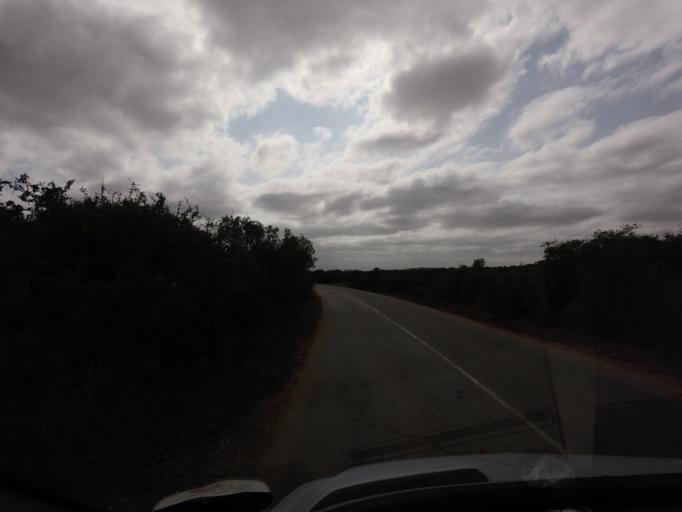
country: ZA
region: Eastern Cape
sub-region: Cacadu District Municipality
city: Kirkwood
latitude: -33.4451
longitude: 25.7358
